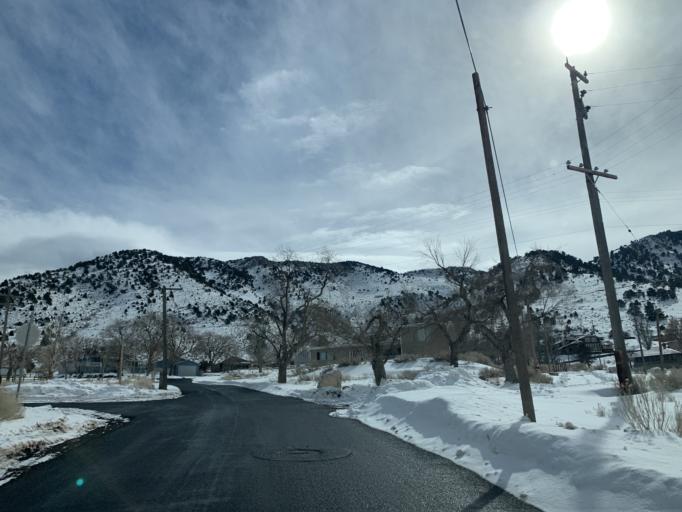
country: US
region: Utah
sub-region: Utah County
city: Genola
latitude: 39.9511
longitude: -112.1160
